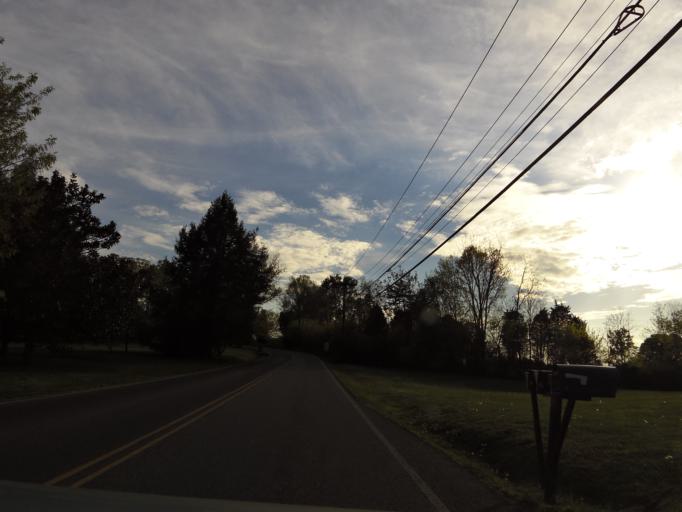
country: US
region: Tennessee
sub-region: Blount County
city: Maryville
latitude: 35.7158
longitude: -84.0088
